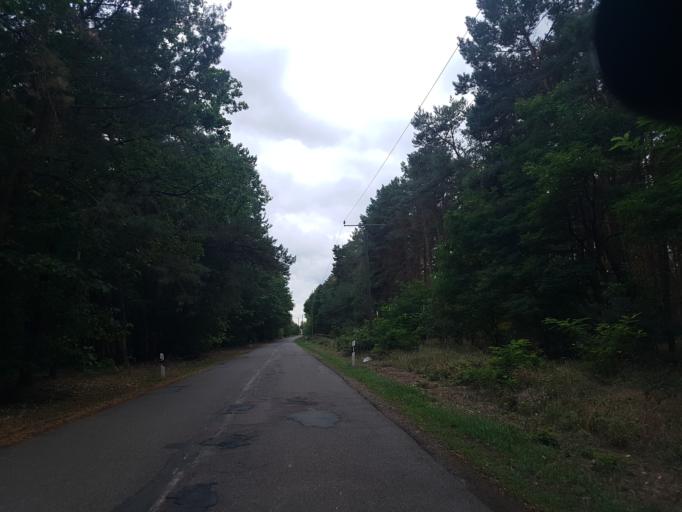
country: DE
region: Saxony-Anhalt
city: Rosslau
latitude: 51.9662
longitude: 12.2999
